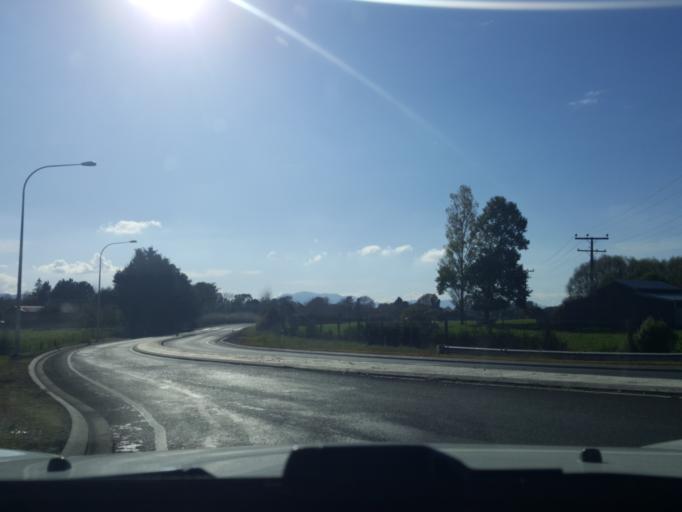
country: NZ
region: Waikato
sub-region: Waikato District
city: Ngaruawahia
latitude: -37.7536
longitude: 175.1532
